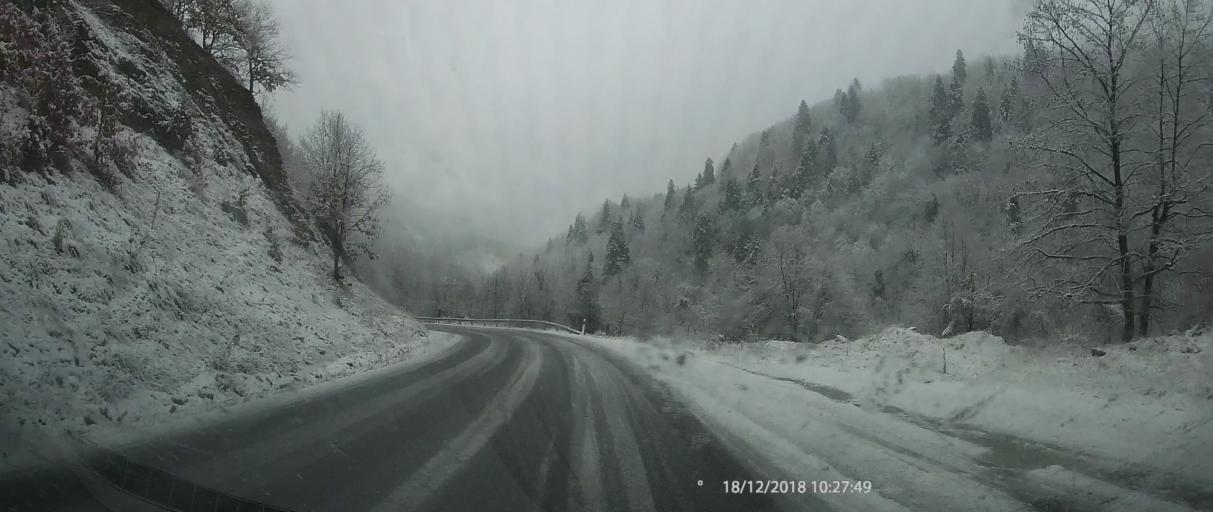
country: GR
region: Thessaly
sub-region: Nomos Larisis
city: Livadi
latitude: 40.1742
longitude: 22.2574
